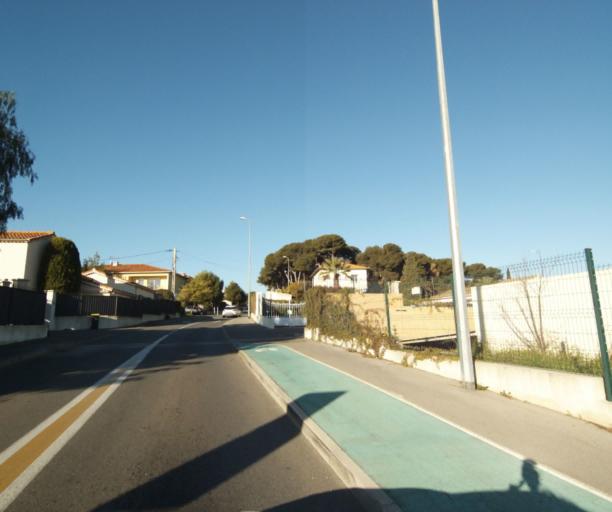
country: FR
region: Provence-Alpes-Cote d'Azur
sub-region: Departement des Alpes-Maritimes
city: Biot
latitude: 43.5960
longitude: 7.0882
